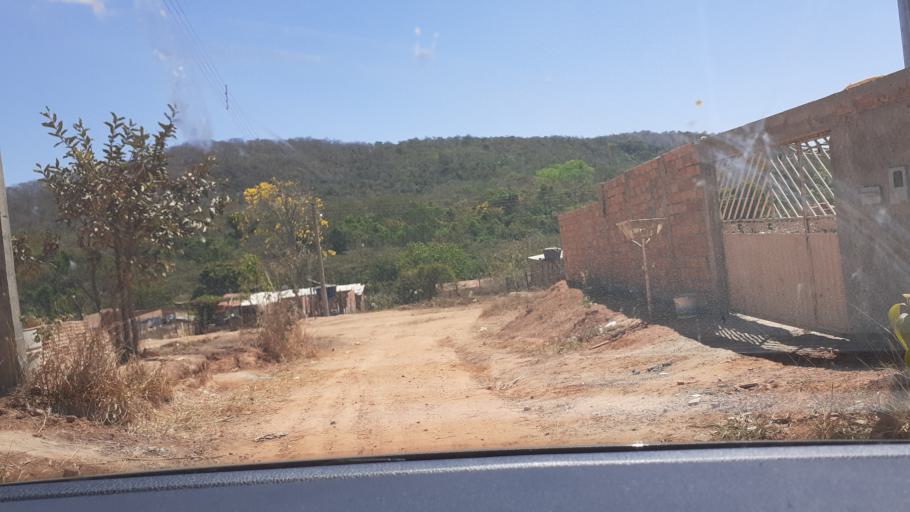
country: BR
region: Goias
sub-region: Caldas Novas
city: Caldas Novas
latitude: -17.7417
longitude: -48.6572
